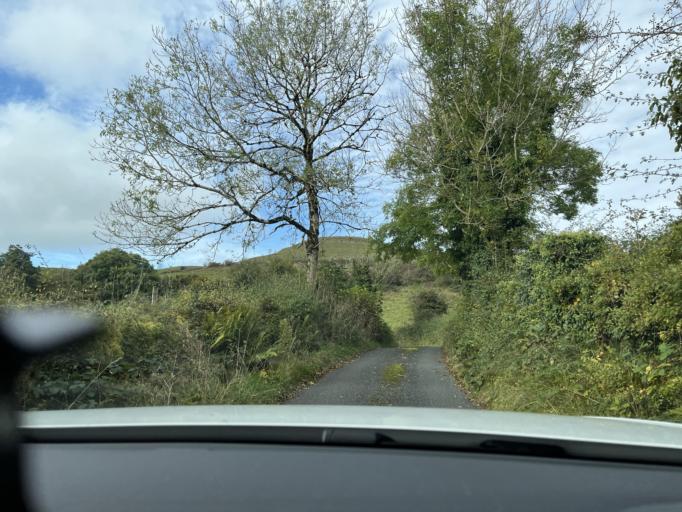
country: IE
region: Connaught
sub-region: Sligo
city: Ballymote
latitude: 54.0479
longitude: -8.4343
